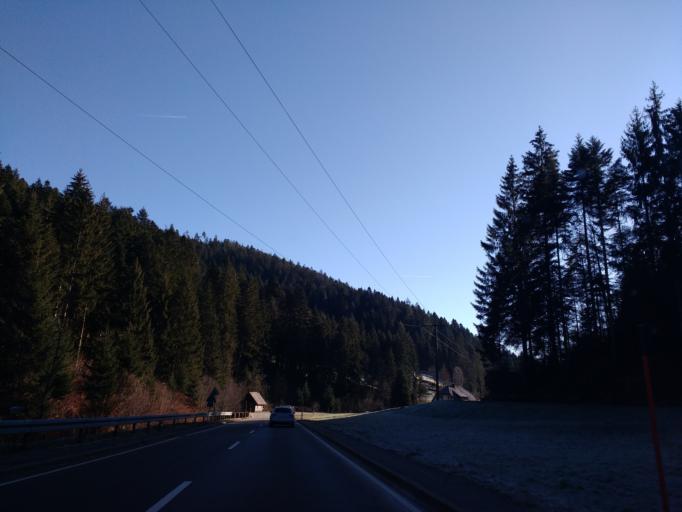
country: DE
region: Baden-Wuerttemberg
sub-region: Karlsruhe Region
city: Bad Rippoldsau-Schapbach
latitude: 48.4437
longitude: 8.3117
